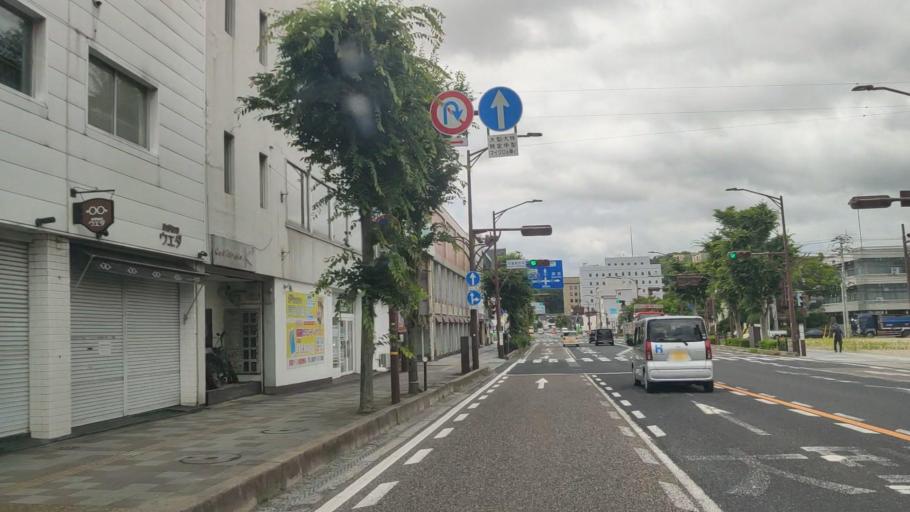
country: JP
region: Tottori
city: Yonago
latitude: 35.4300
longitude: 133.3316
